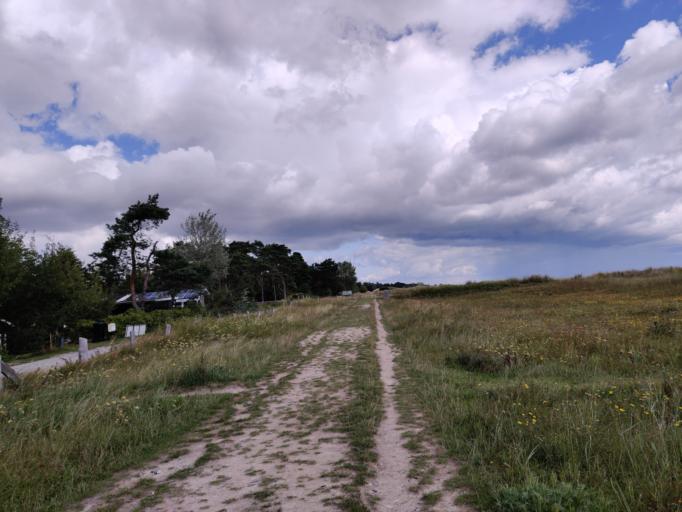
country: DK
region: Zealand
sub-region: Guldborgsund Kommune
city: Nykobing Falster
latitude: 54.7045
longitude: 11.9809
